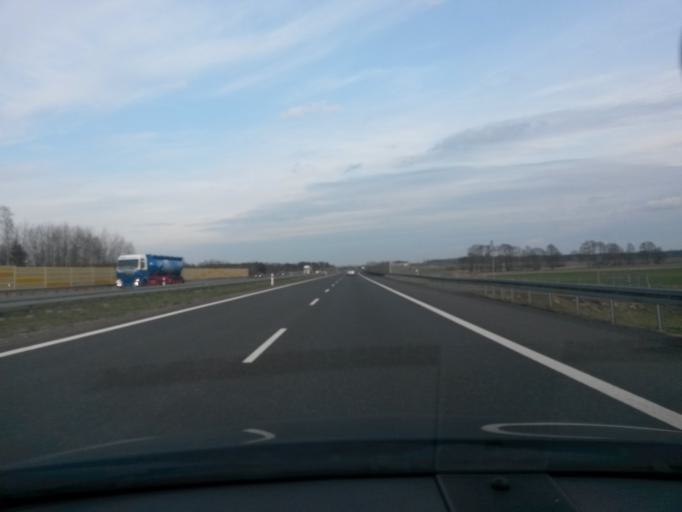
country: PL
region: Lodz Voivodeship
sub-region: Powiat zgierski
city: Parzeczew
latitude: 51.9531
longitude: 19.1490
